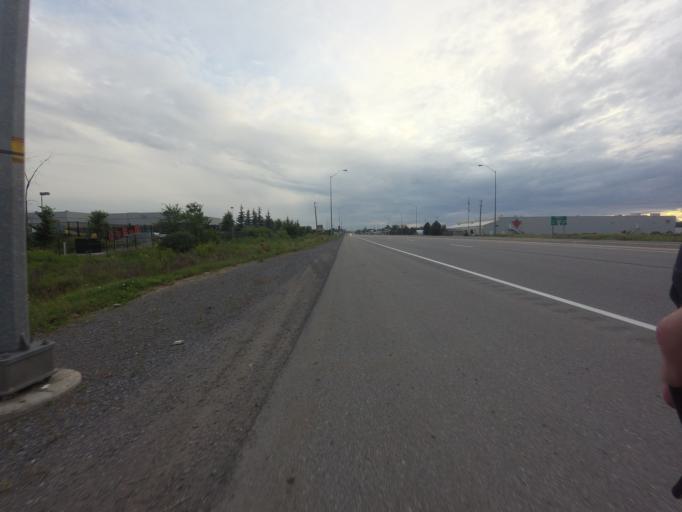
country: CA
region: Ontario
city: Carleton Place
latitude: 45.1341
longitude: -76.1168
